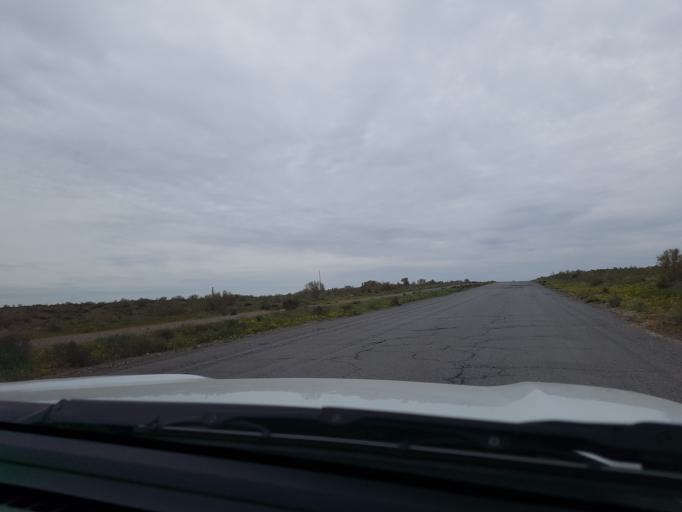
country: TM
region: Mary
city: Bayramaly
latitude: 37.8872
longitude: 62.6147
